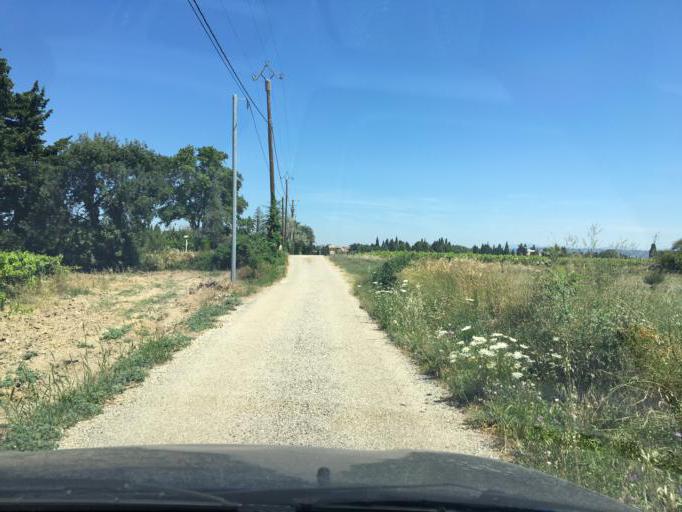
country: FR
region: Provence-Alpes-Cote d'Azur
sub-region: Departement du Vaucluse
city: Camaret-sur-Aigues
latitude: 44.1749
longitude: 4.8957
